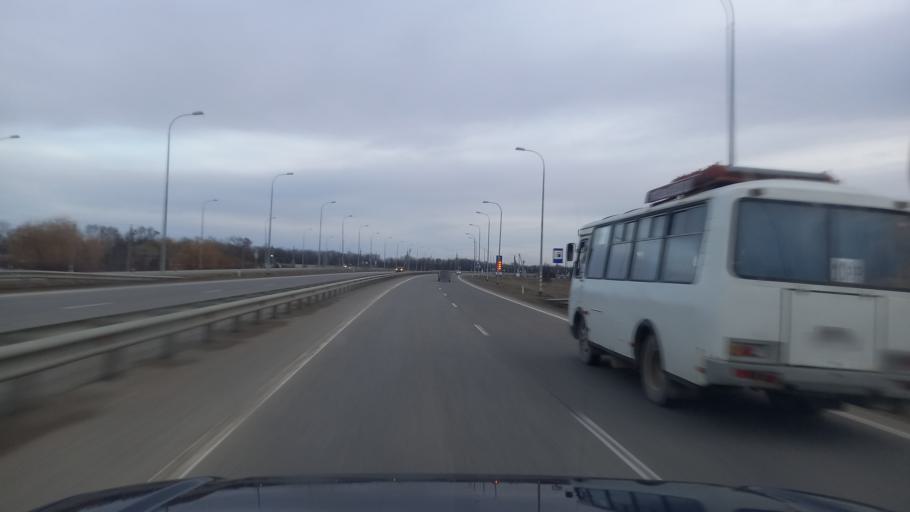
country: RU
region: Adygeya
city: Khanskaya
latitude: 44.6839
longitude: 39.9864
